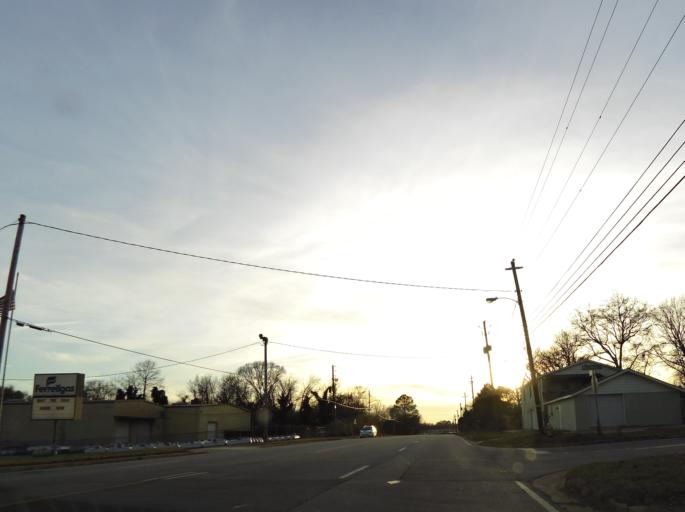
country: US
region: Georgia
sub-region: Bibb County
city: Macon
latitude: 32.7942
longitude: -83.6448
